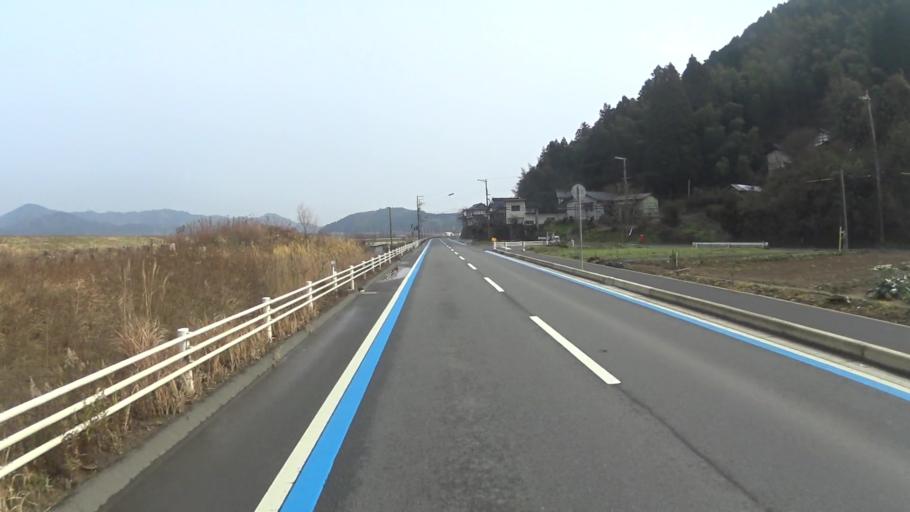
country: JP
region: Kyoto
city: Fukuchiyama
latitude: 35.3791
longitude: 135.1432
